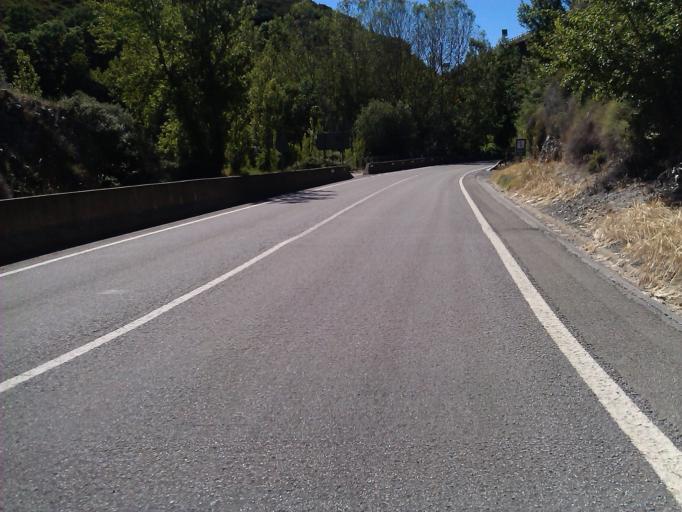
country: ES
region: Castille and Leon
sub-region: Provincia de Leon
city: Trabadelo
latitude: 42.6554
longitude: -6.9040
